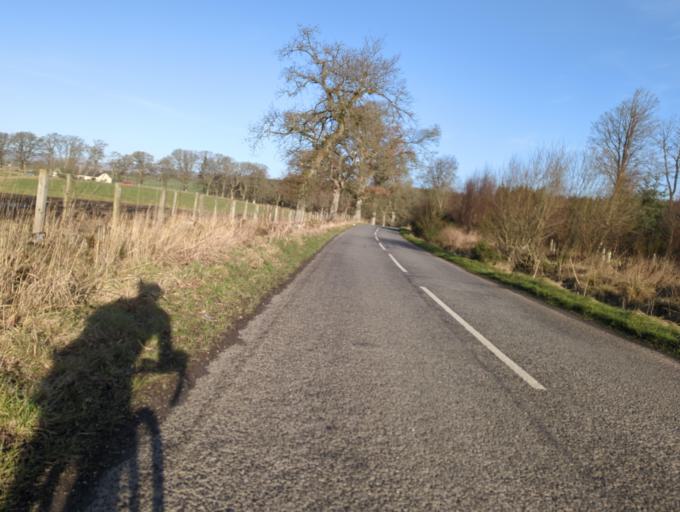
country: GB
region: Scotland
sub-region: Perth and Kinross
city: Methven
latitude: 56.4568
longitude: -3.5854
